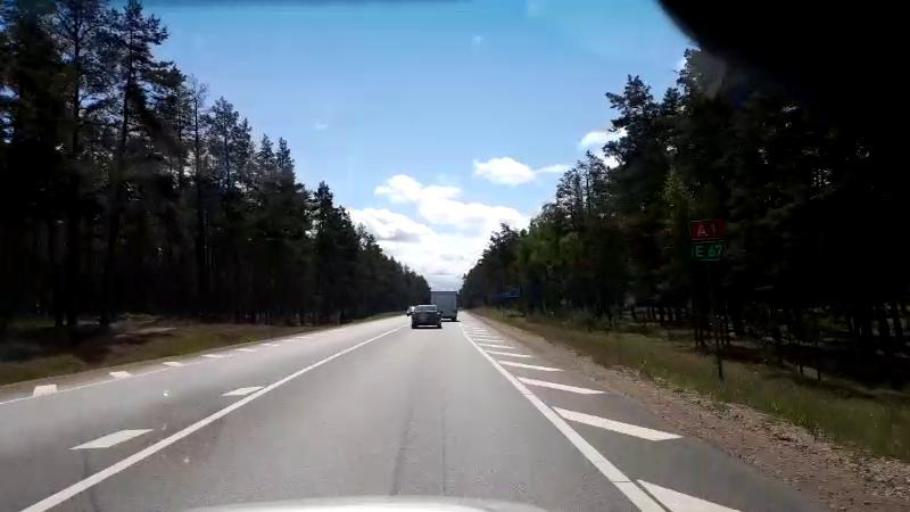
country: LV
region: Carnikava
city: Carnikava
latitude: 57.1701
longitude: 24.3436
